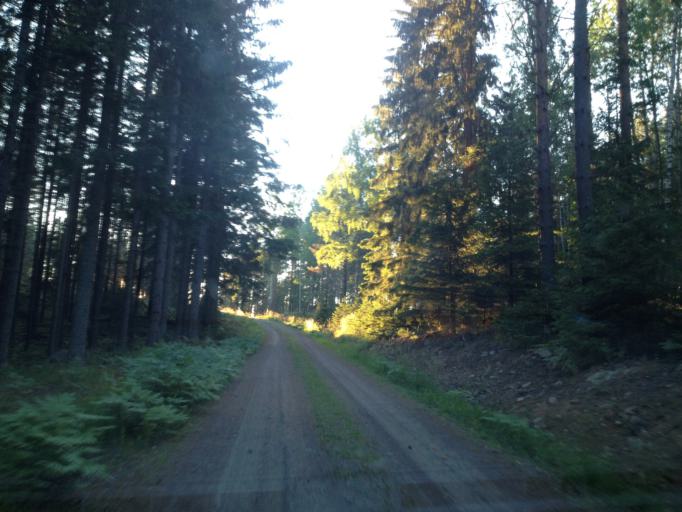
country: SE
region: Kalmar
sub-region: Vasterviks Kommun
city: Overum
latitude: 57.9988
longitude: 16.1339
